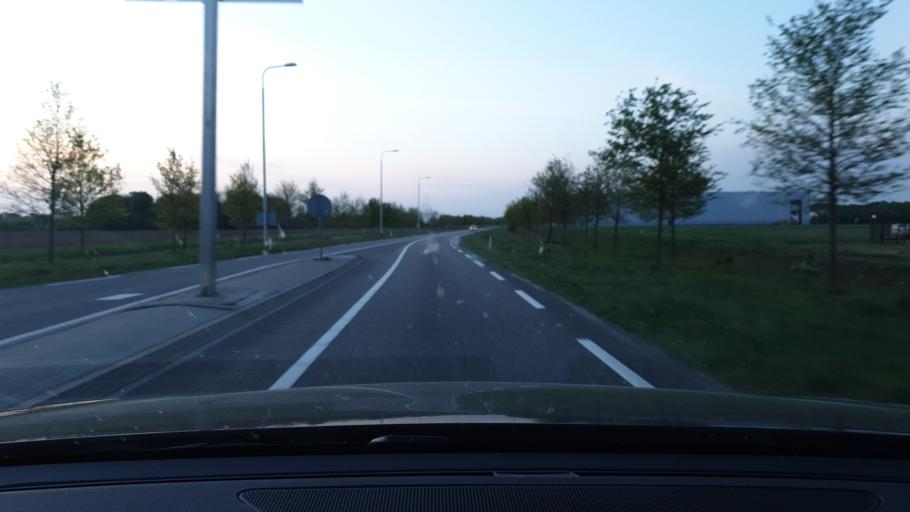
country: NL
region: North Brabant
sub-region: Gemeente Eersel
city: Eersel
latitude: 51.3563
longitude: 5.2719
